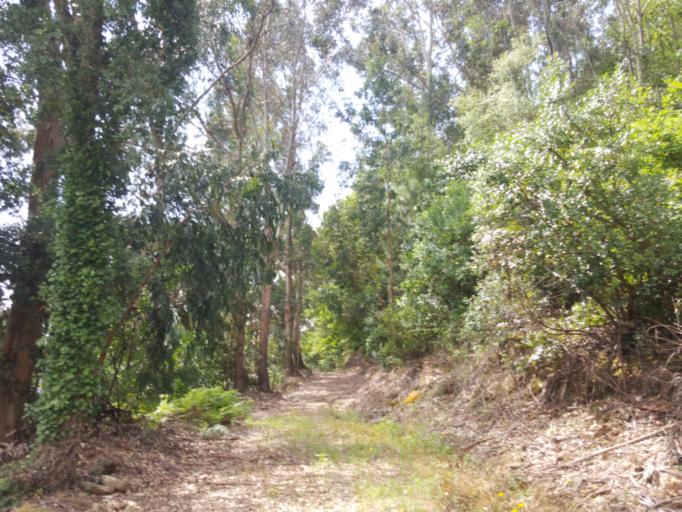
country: PT
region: Vila Real
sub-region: Mesao Frio
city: Mesao Frio
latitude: 41.1746
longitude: -7.8440
